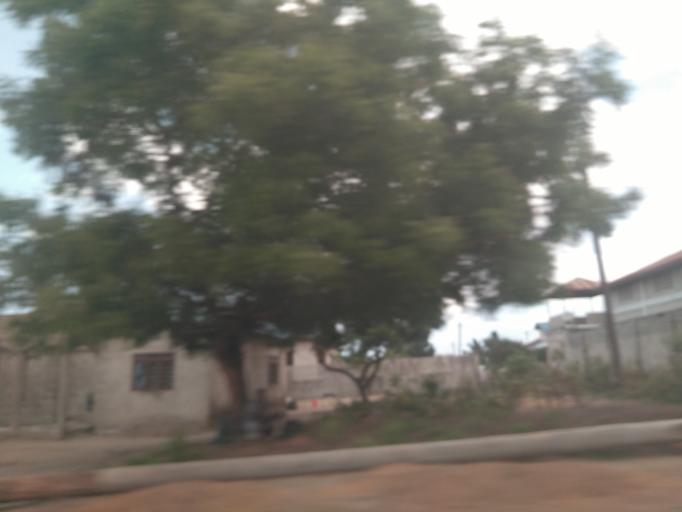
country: TZ
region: Dar es Salaam
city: Dar es Salaam
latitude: -6.8955
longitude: 39.2836
